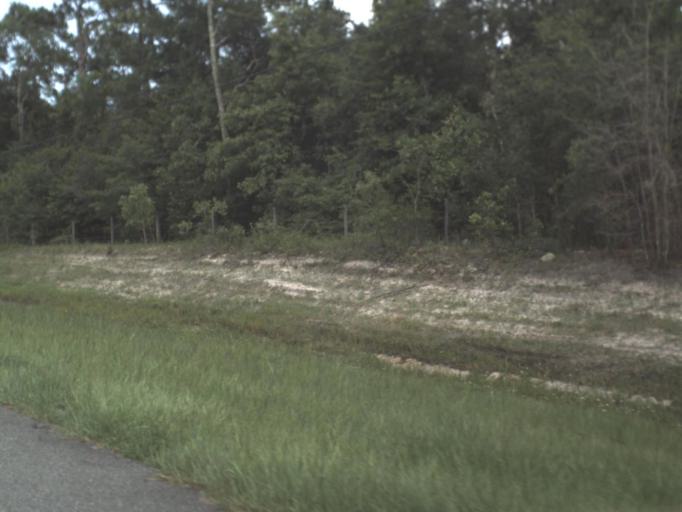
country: US
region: Florida
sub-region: Clay County
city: Asbury Lake
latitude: 29.9821
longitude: -81.8408
